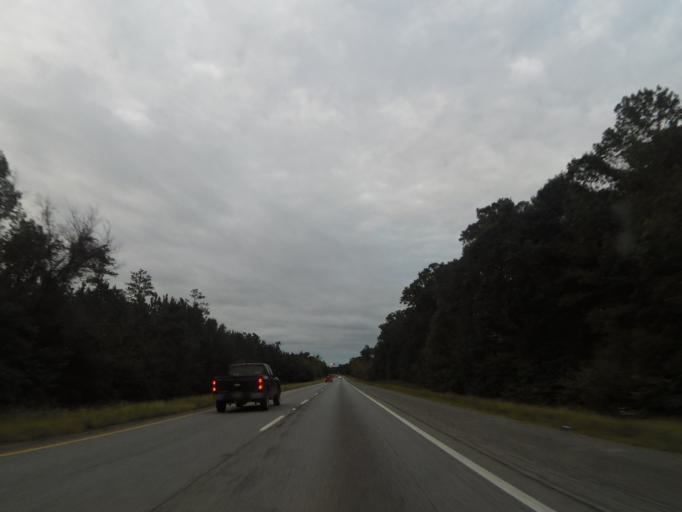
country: US
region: Alabama
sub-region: Saint Clair County
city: Steele
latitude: 33.9179
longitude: -86.2131
